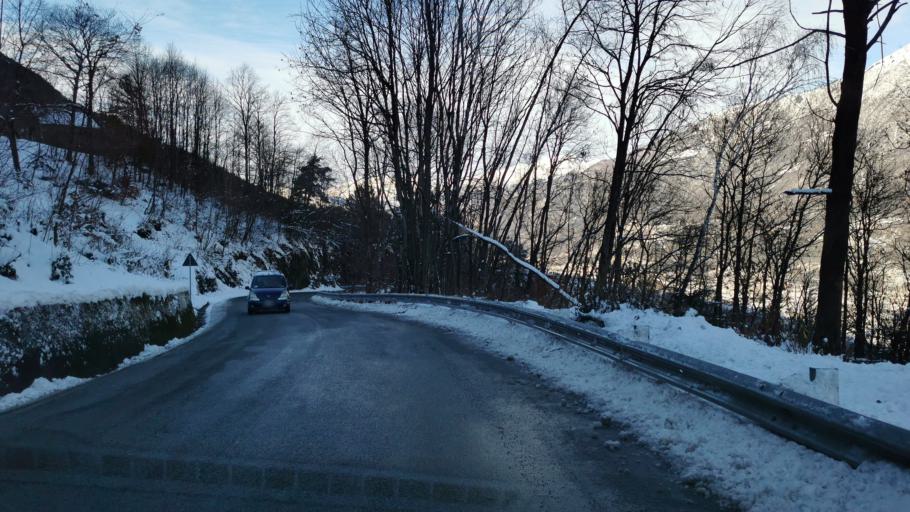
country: IT
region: Lombardy
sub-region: Provincia di Sondrio
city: Regoledo
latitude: 46.1242
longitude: 9.5385
